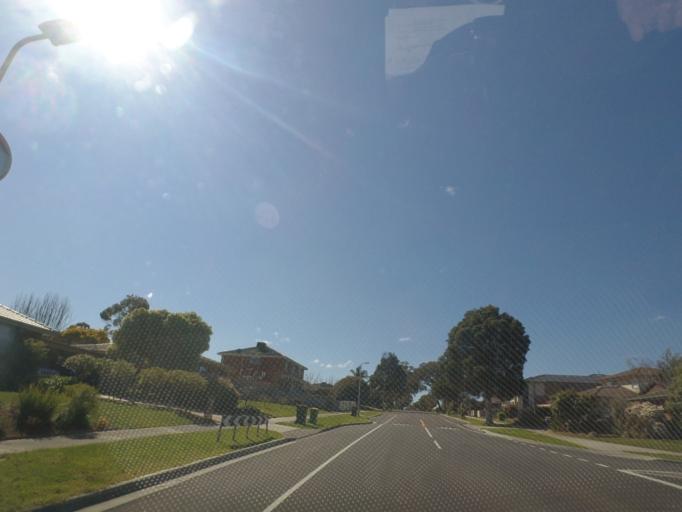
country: AU
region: Victoria
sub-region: Knox
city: Wantirna South
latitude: -37.8795
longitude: 145.2232
